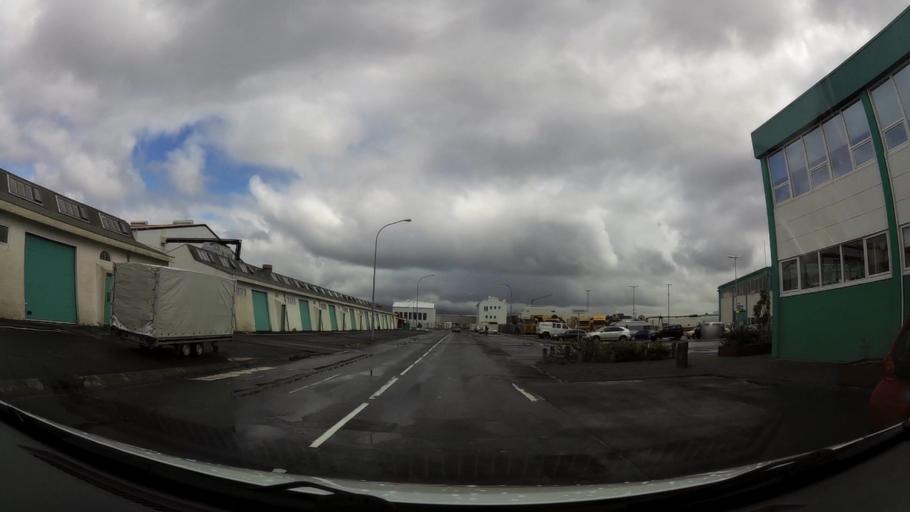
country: IS
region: Capital Region
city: Seltjarnarnes
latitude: 64.1549
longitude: -21.9436
